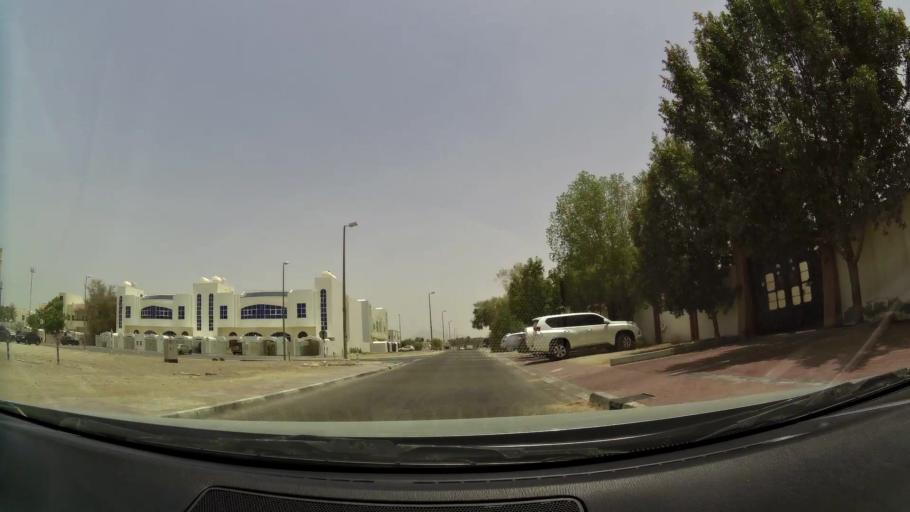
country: AE
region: Abu Dhabi
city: Al Ain
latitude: 24.2167
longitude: 55.7216
